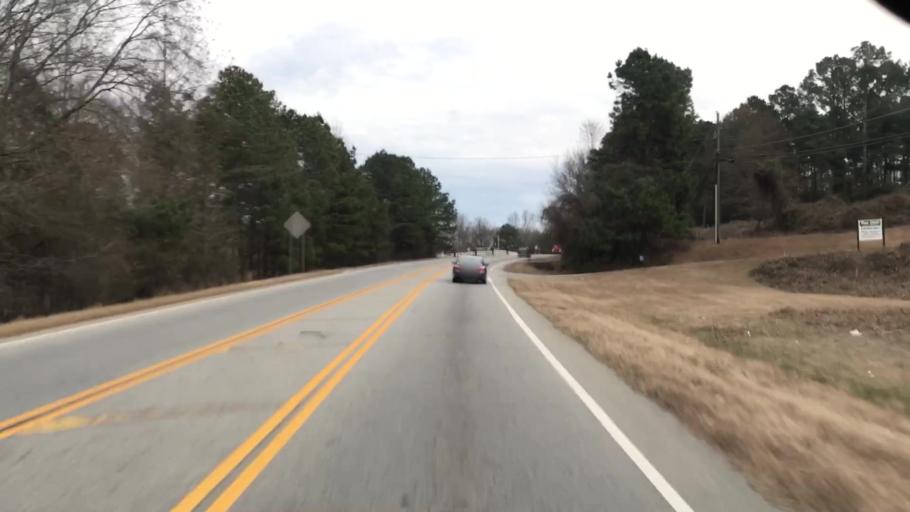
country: US
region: Georgia
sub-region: Barrow County
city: Winder
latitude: 34.0044
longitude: -83.7529
